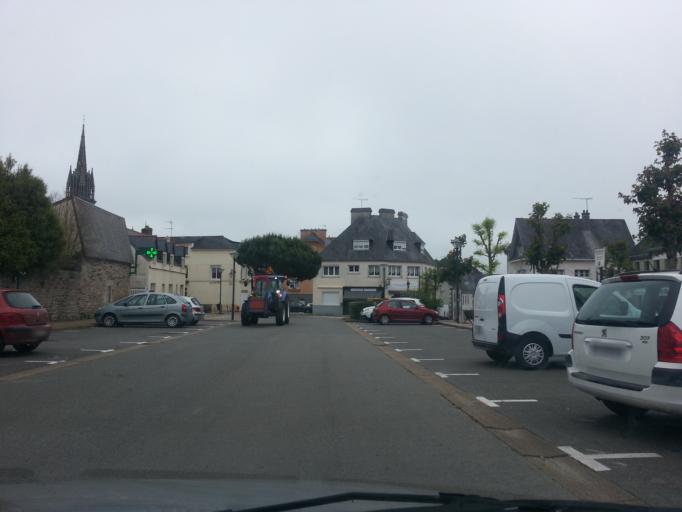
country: FR
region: Brittany
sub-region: Departement du Finistere
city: Scaer
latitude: 48.0270
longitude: -3.7021
